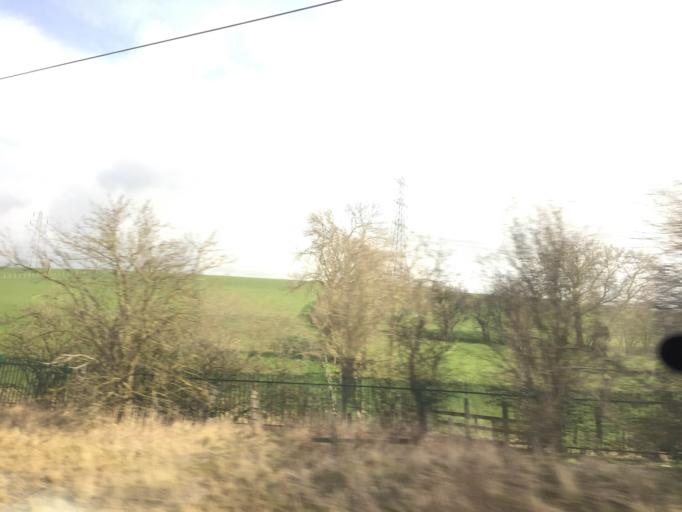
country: GB
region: England
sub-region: Cumbria
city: Penrith
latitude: 54.5677
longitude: -2.6831
